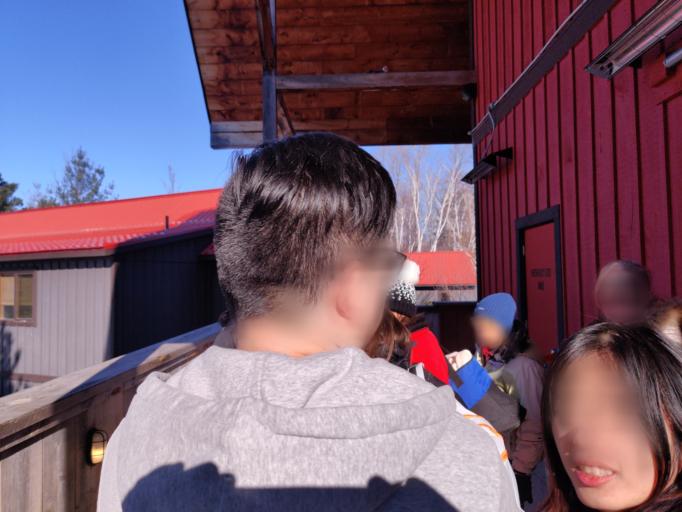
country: CA
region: Ontario
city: Collingwood
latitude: 44.5016
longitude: -80.2902
